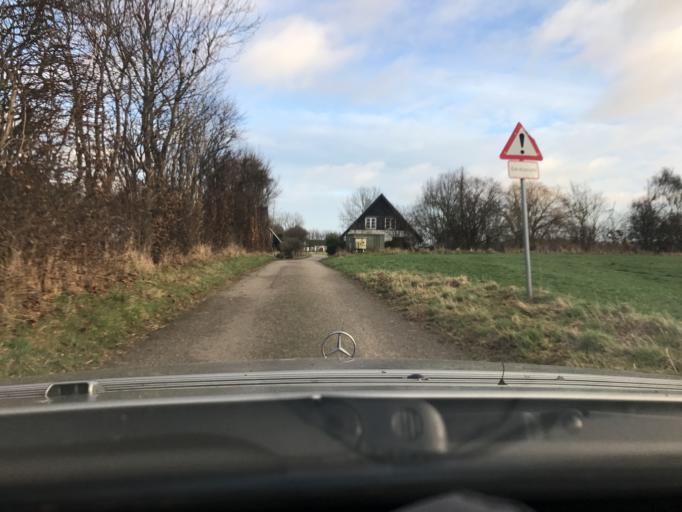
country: DK
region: South Denmark
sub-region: Sonderborg Kommune
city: Nordborg
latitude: 55.0517
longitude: 9.6564
